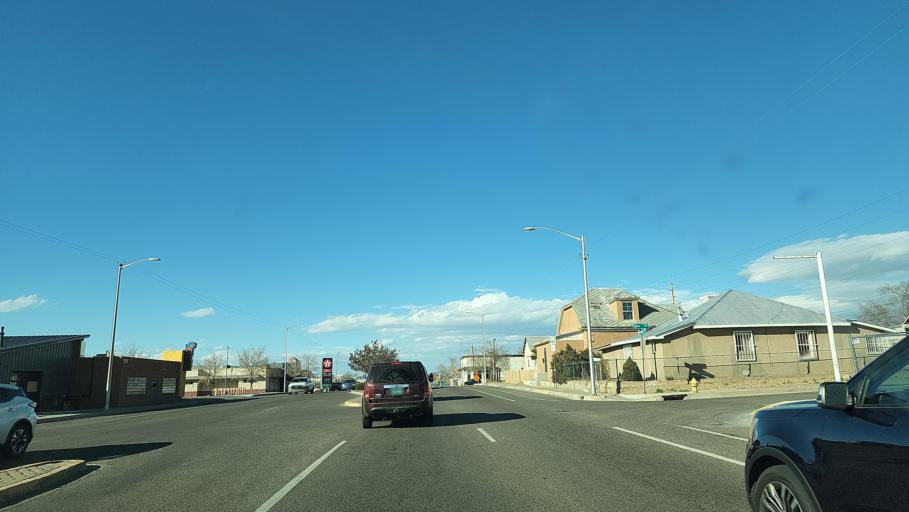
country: US
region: New Mexico
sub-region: Bernalillo County
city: Albuquerque
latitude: 35.0674
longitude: -106.6455
